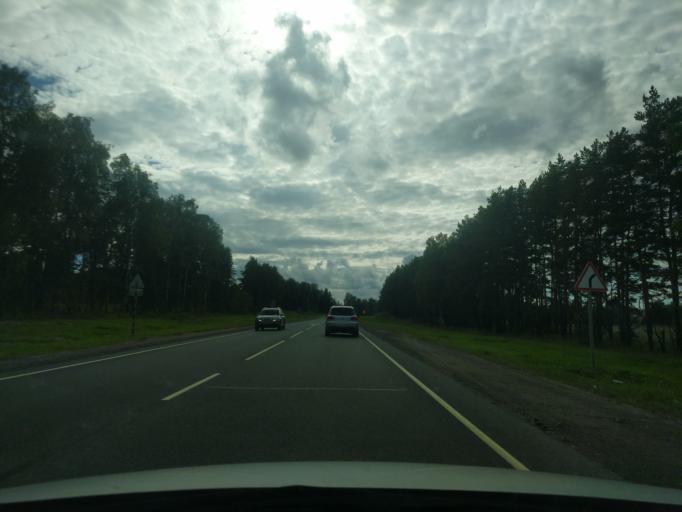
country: RU
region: Jaroslavl
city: Levashevo
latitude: 57.6487
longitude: 40.5477
